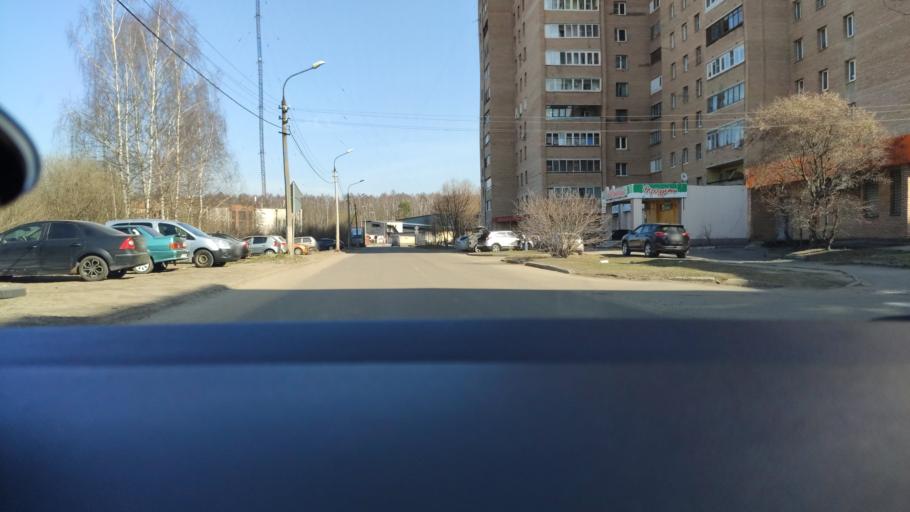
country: RU
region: Moskovskaya
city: Elektrostal'
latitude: 55.7724
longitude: 38.4192
